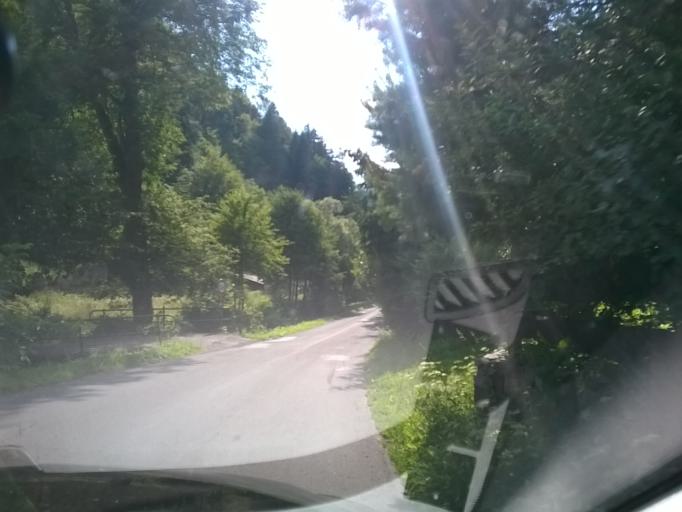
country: SK
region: Banskobystricky
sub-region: Okres Banska Bystrica
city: Banska Stiavnica
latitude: 48.4618
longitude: 18.8238
